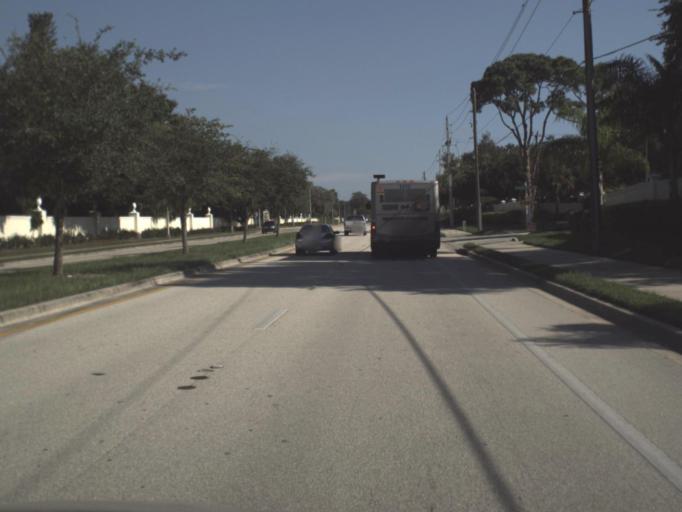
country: US
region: Florida
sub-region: Sarasota County
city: Englewood
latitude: 26.9972
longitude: -82.3740
